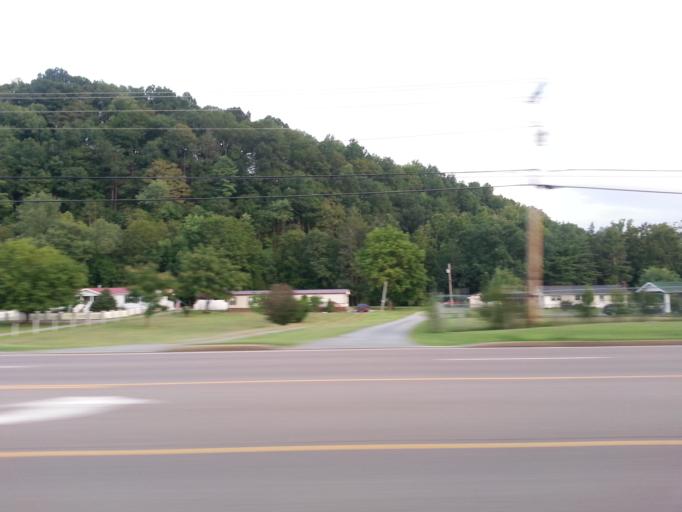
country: US
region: Tennessee
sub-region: Carter County
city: Hunter
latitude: 36.3919
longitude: -82.1241
